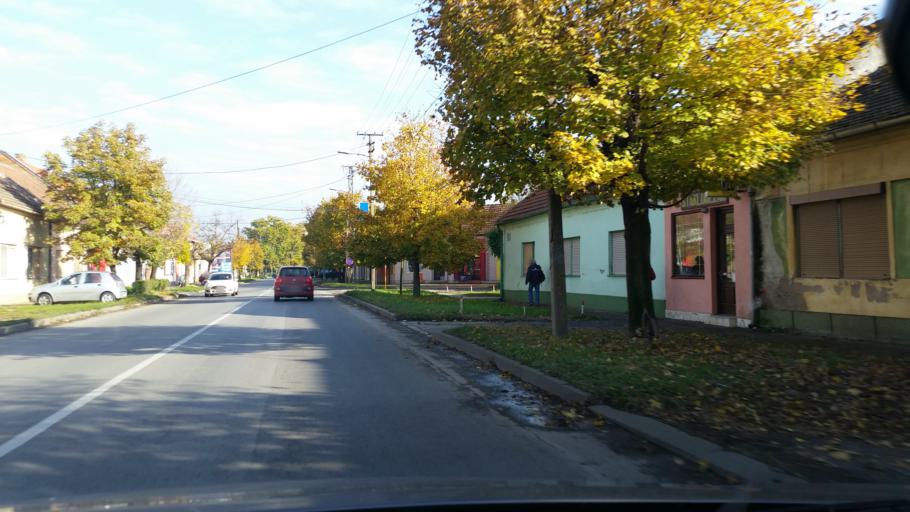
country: RS
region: Autonomna Pokrajina Vojvodina
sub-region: Srednjebanatski Okrug
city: Zrenjanin
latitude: 45.3775
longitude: 20.4054
